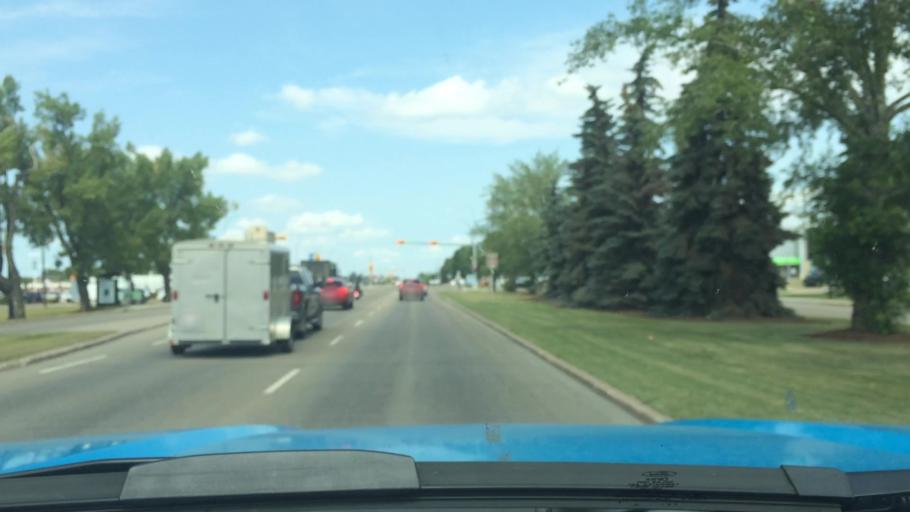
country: CA
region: Alberta
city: Red Deer
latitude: 52.2473
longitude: -113.8139
